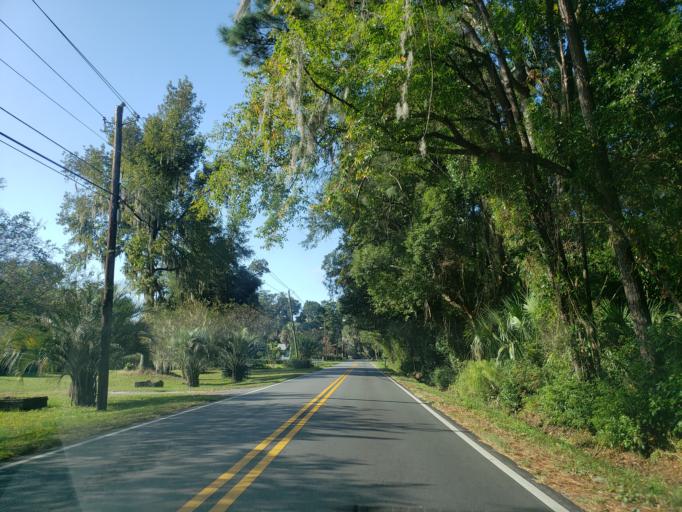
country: US
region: Georgia
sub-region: Chatham County
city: Montgomery
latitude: 31.9474
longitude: -81.1079
